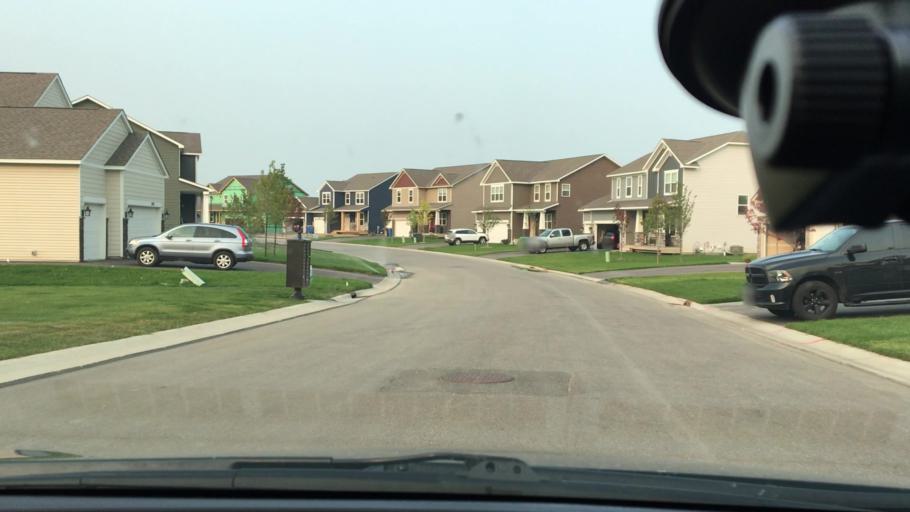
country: US
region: Minnesota
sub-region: Wright County
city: Saint Michael
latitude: 45.2034
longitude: -93.6820
